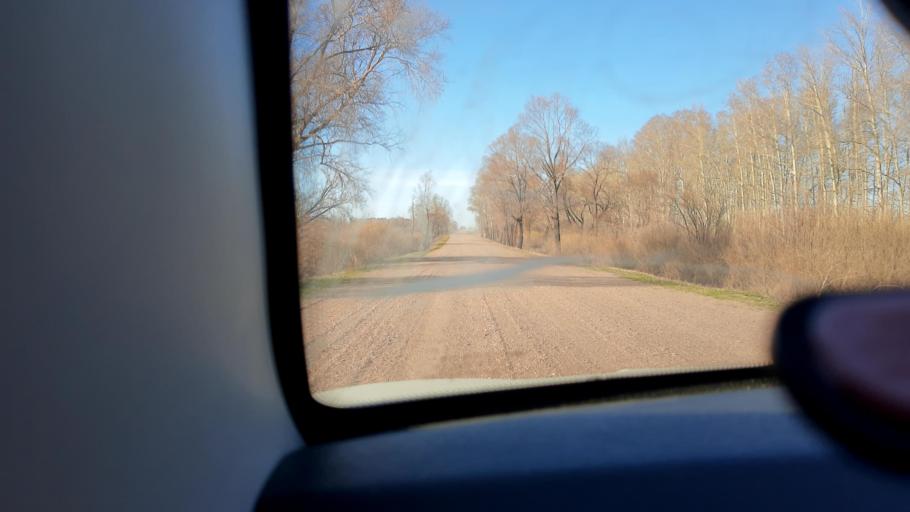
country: RU
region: Bashkortostan
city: Asanovo
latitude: 54.8609
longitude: 55.4613
